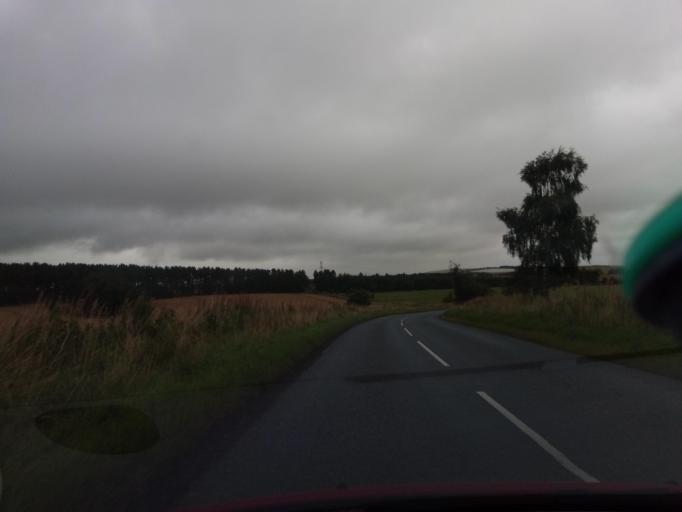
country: GB
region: Scotland
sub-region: The Scottish Borders
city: Earlston
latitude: 55.6596
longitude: -2.5528
